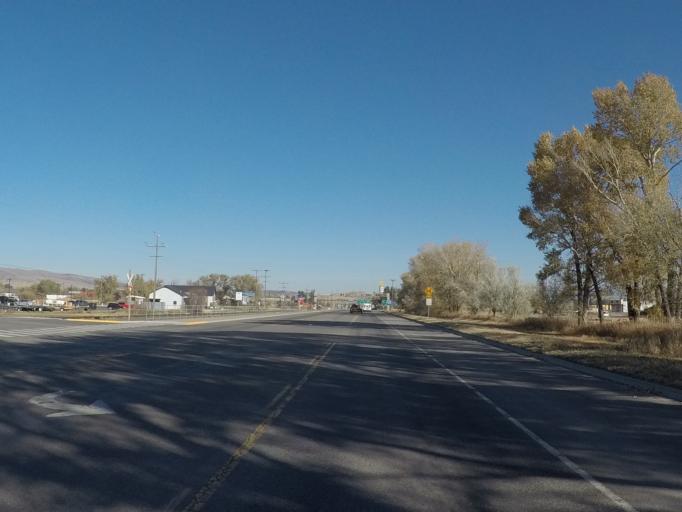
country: US
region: Montana
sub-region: Park County
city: Livingston
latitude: 45.6379
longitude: -110.5749
